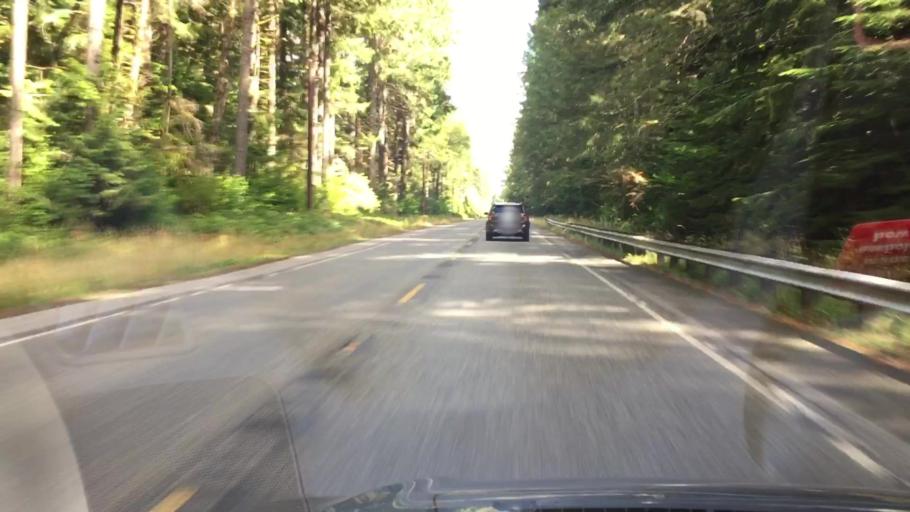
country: US
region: Washington
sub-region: Pierce County
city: Eatonville
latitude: 46.7562
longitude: -122.0786
